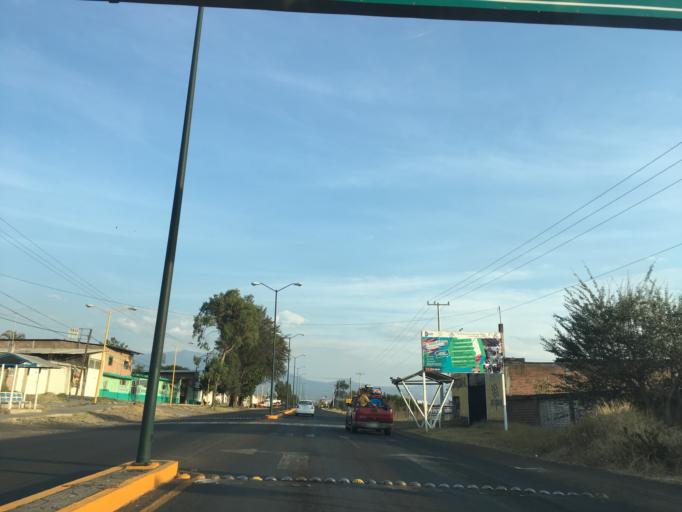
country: MX
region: Michoacan
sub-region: Los Reyes
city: La Higuerita (Colonia San Rafael)
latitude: 19.6136
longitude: -102.4828
